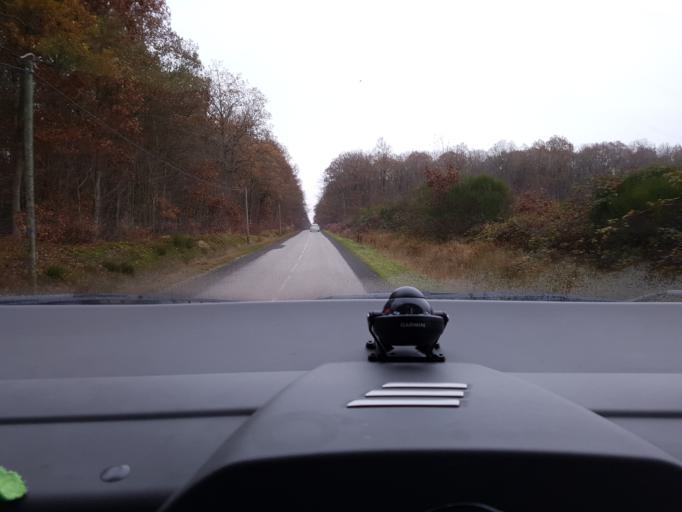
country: FR
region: Haute-Normandie
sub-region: Departement de l'Eure
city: Rugles
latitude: 48.9452
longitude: 0.7543
